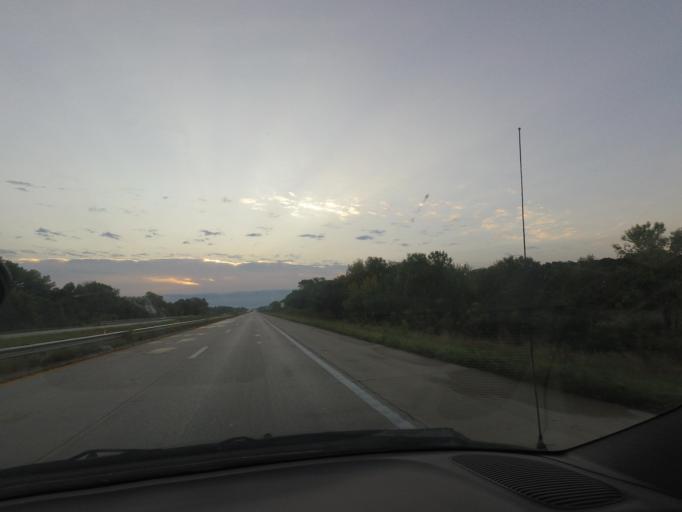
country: US
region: Missouri
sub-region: Macon County
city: Macon
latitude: 39.7534
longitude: -92.4154
